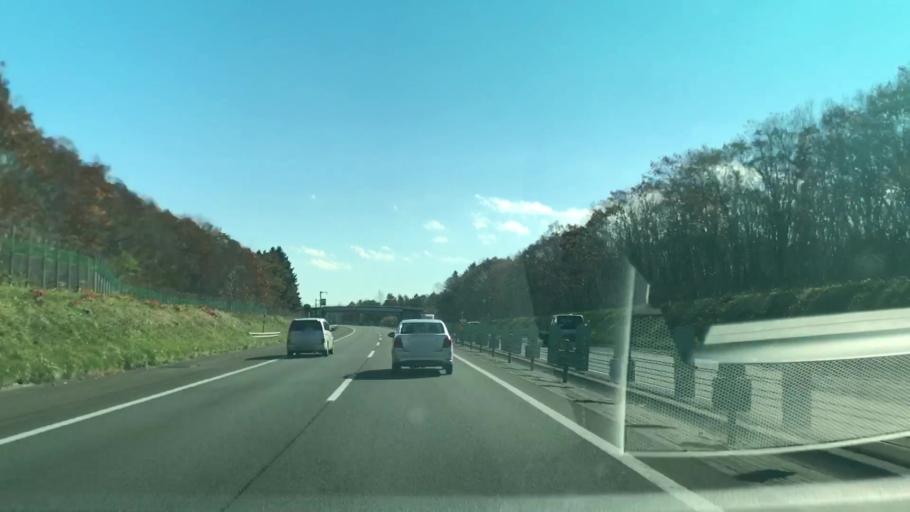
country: JP
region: Hokkaido
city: Chitose
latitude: 42.8597
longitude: 141.5601
